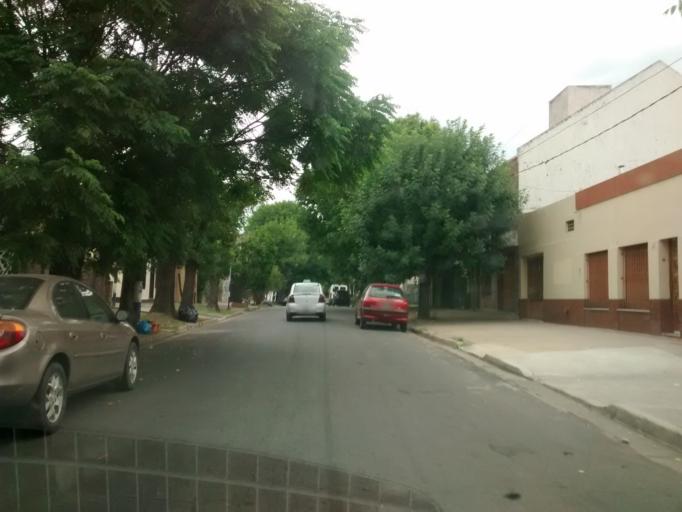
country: AR
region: Buenos Aires
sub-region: Partido de La Plata
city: La Plata
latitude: -34.9309
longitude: -57.9236
